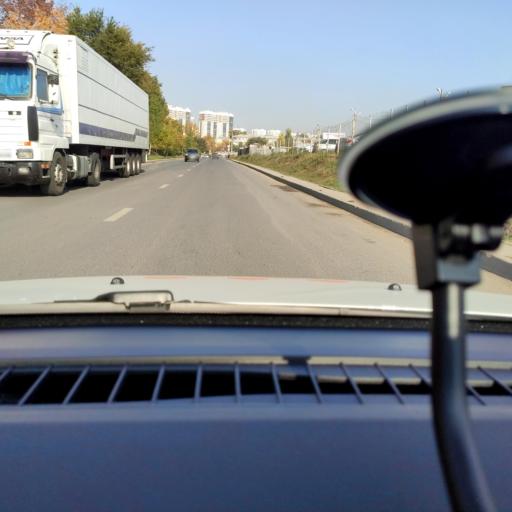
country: RU
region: Samara
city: Samara
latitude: 53.2087
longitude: 50.1939
